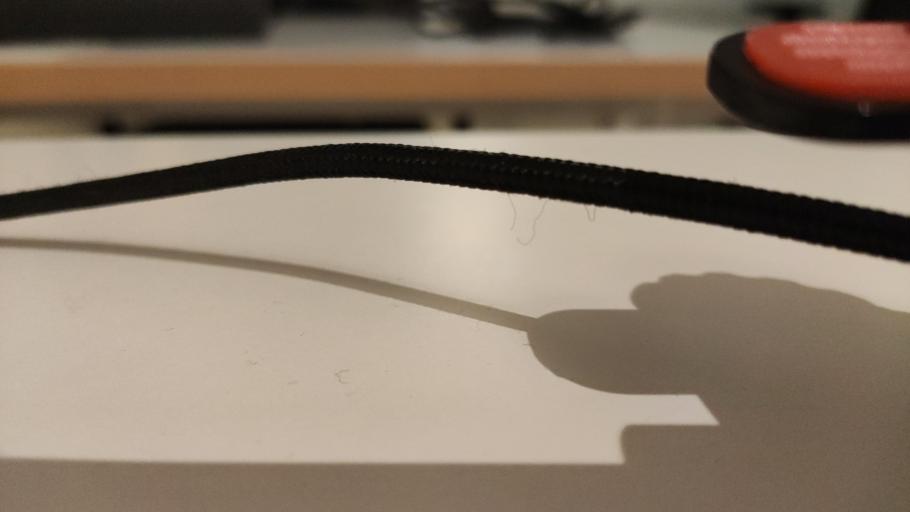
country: RU
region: Moskovskaya
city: Novoye
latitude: 55.6068
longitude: 38.9276
